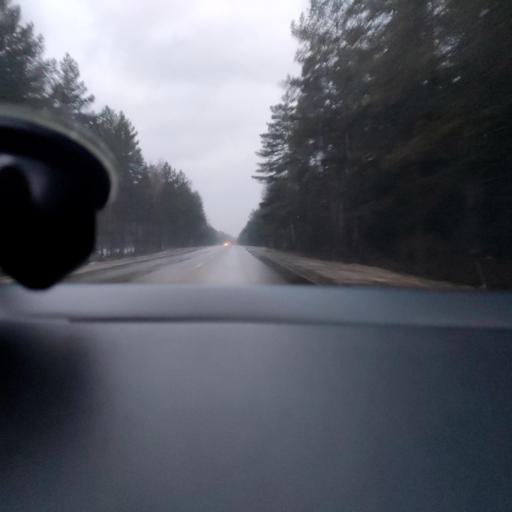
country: RU
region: Moskovskaya
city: Krasnyy Tkach
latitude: 55.4095
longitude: 39.1639
